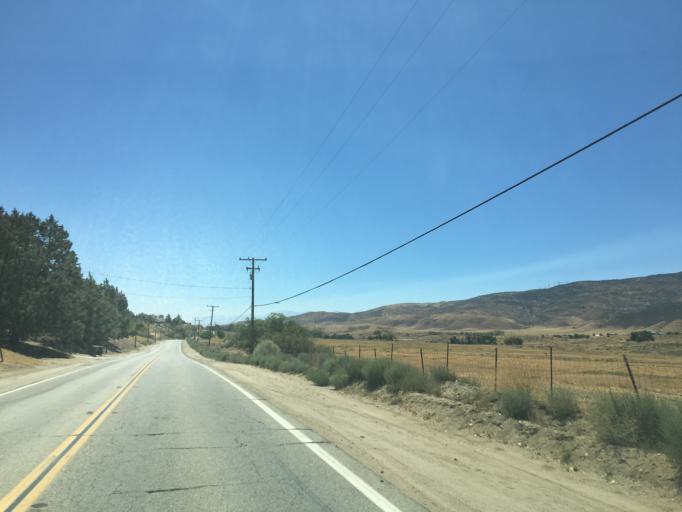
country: US
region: California
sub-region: Los Angeles County
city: Leona Valley
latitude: 34.6150
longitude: -118.2801
